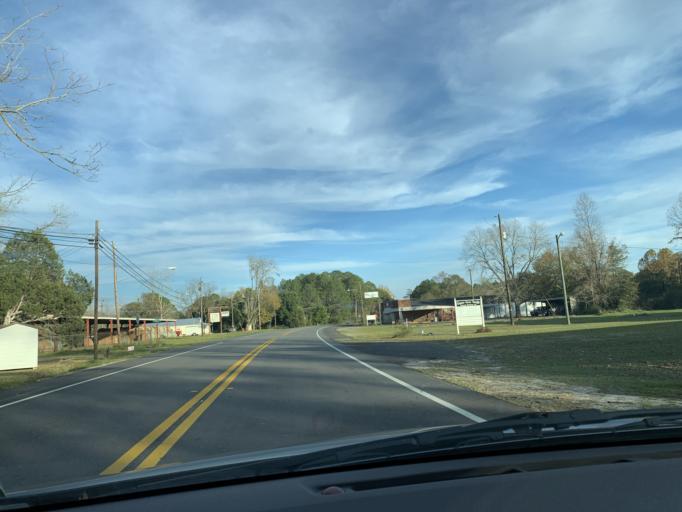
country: US
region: Georgia
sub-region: Irwin County
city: Ocilla
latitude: 31.5941
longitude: -83.2413
